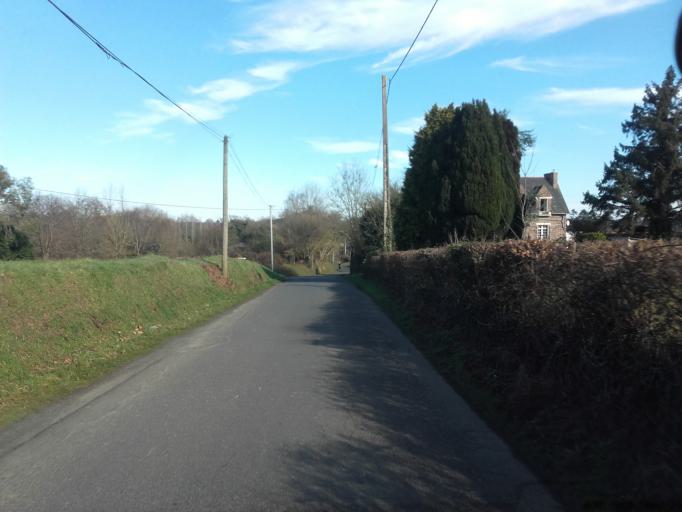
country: FR
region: Brittany
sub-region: Departement des Cotes-d'Armor
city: Plouha
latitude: 48.6615
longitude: -2.9334
